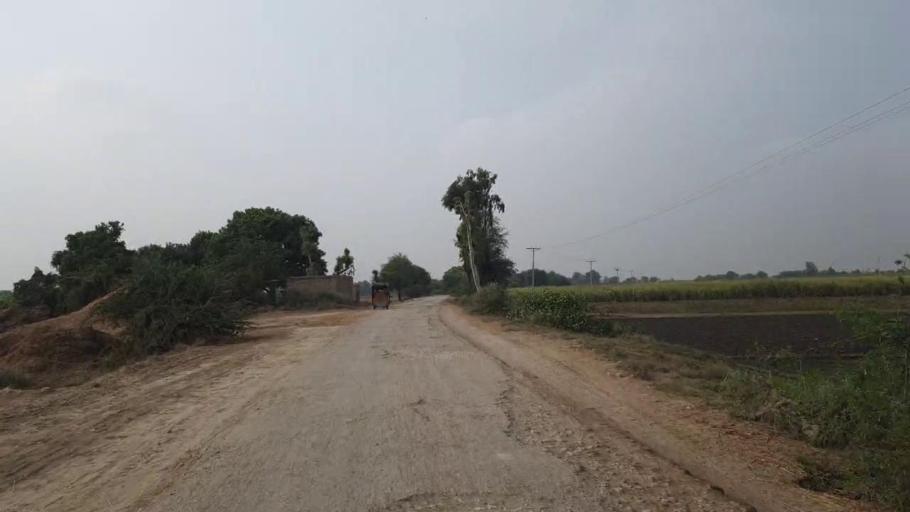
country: PK
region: Sindh
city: Matli
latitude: 24.9815
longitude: 68.6233
